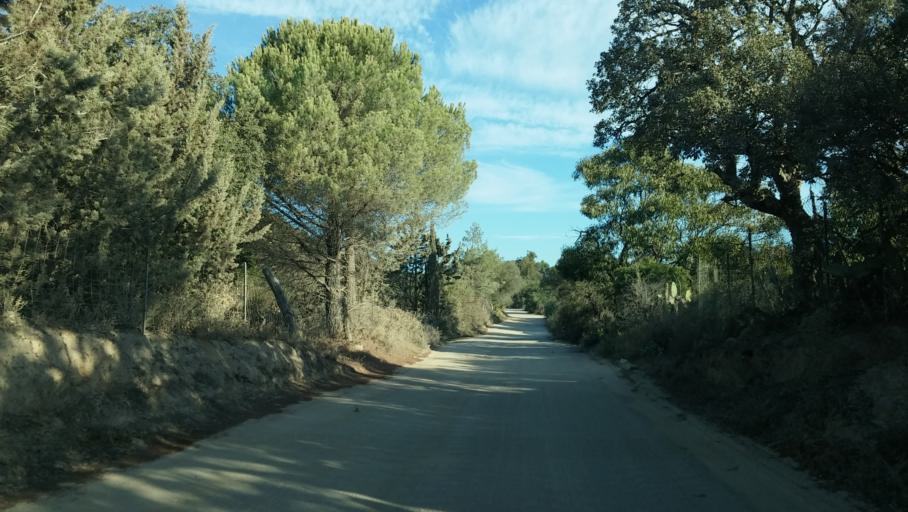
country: IT
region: Sardinia
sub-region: Provincia di Nuoro
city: La Caletta
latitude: 40.4847
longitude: 9.8016
